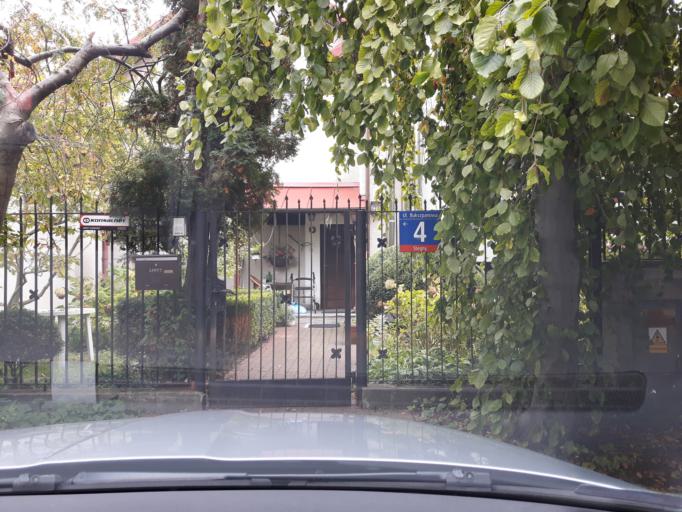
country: PL
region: Masovian Voivodeship
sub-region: Warszawa
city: Mokotow
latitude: 52.1854
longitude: 21.0352
